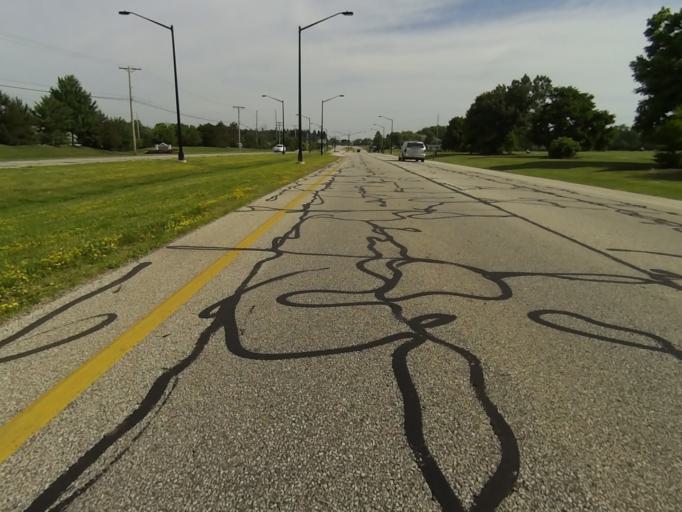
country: US
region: Ohio
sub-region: Summit County
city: Hudson
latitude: 41.2155
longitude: -81.4405
